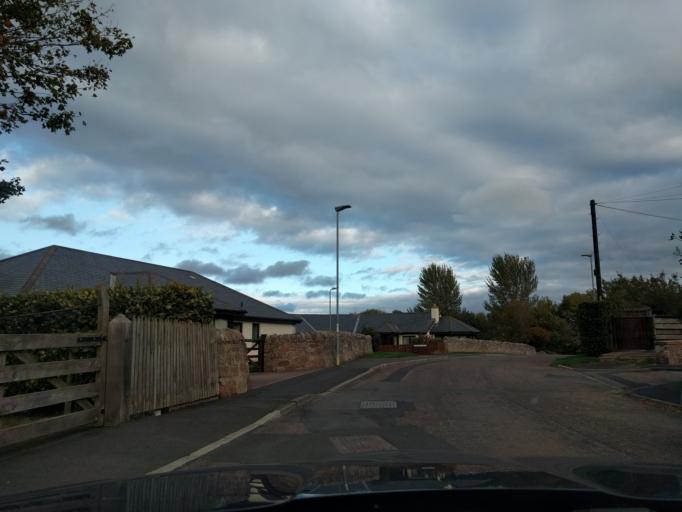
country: GB
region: Scotland
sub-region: The Scottish Borders
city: Allanton
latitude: 55.7427
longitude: -2.1120
